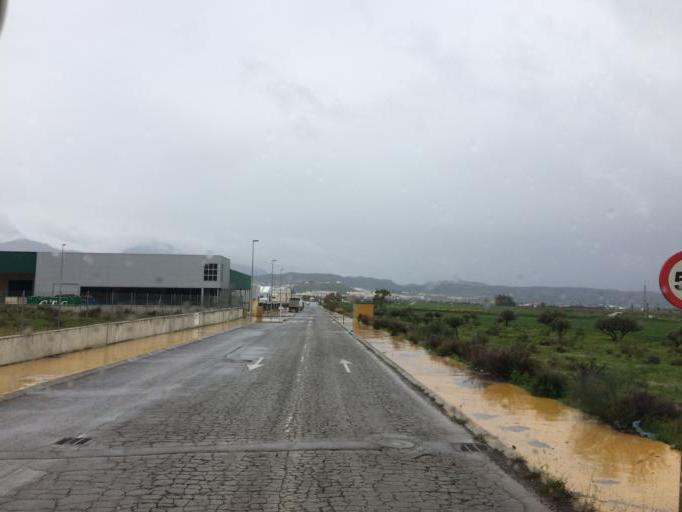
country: ES
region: Andalusia
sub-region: Provincia de Malaga
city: Antequera
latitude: 37.0458
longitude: -4.5207
